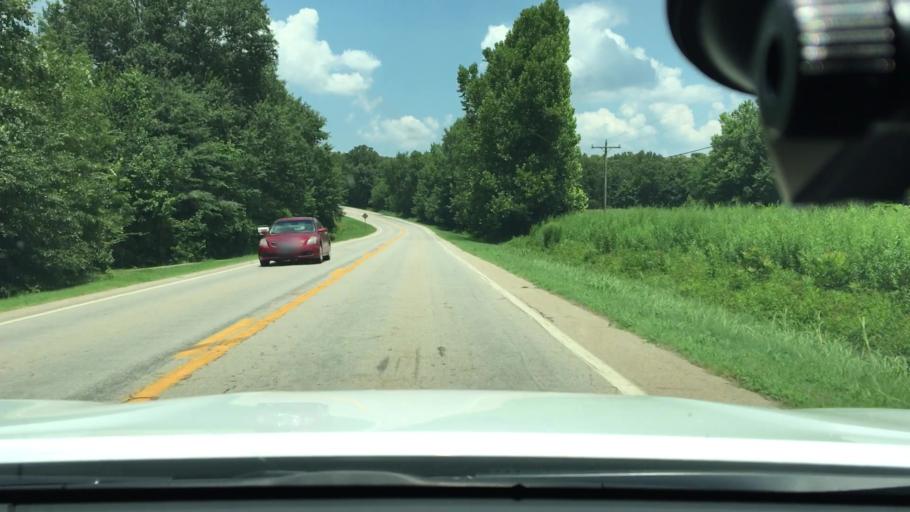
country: US
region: Arkansas
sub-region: Logan County
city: Booneville
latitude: 35.2063
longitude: -93.9244
